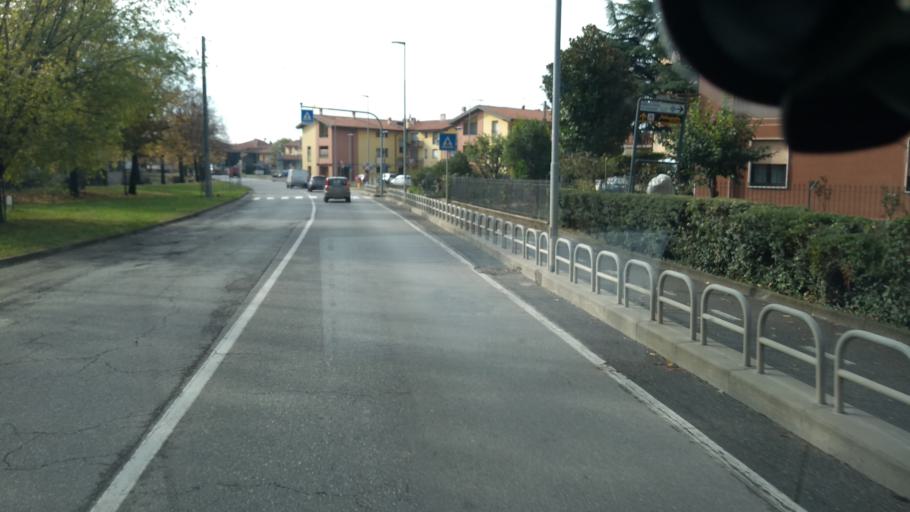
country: IT
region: Lombardy
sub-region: Provincia di Bergamo
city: Cologno al Serio
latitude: 45.5806
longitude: 9.7047
